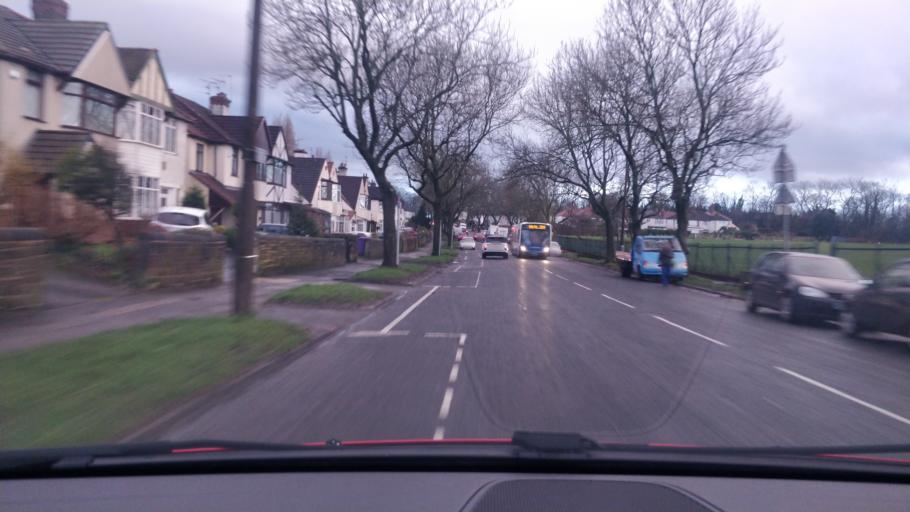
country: GB
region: England
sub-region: Knowsley
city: Huyton
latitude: 53.4144
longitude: -2.8920
